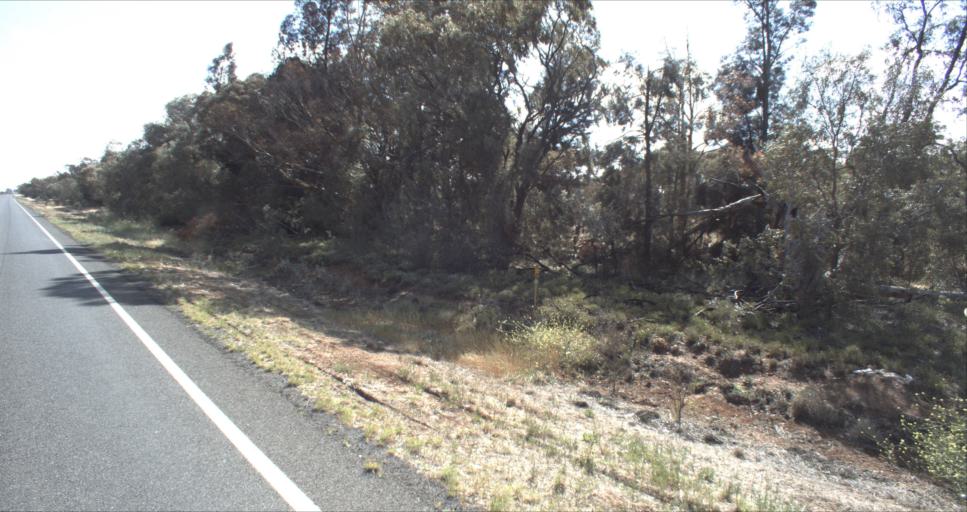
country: AU
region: New South Wales
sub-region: Murrumbidgee Shire
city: Darlington Point
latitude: -34.5291
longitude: 146.1743
